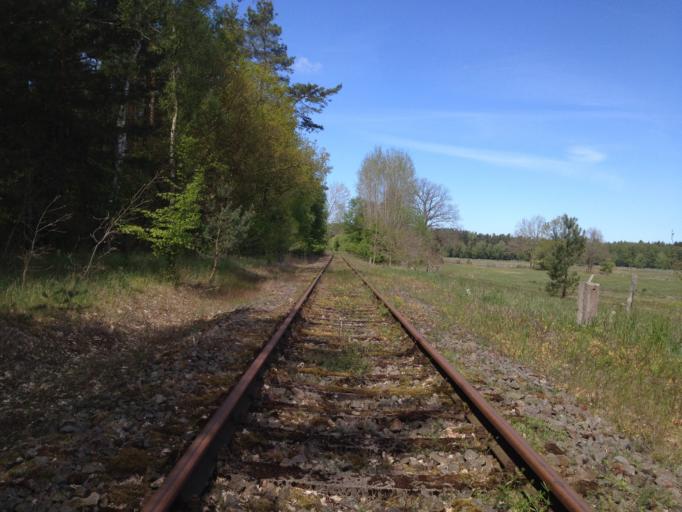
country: DE
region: Brandenburg
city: Templin
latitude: 53.1373
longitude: 13.4277
